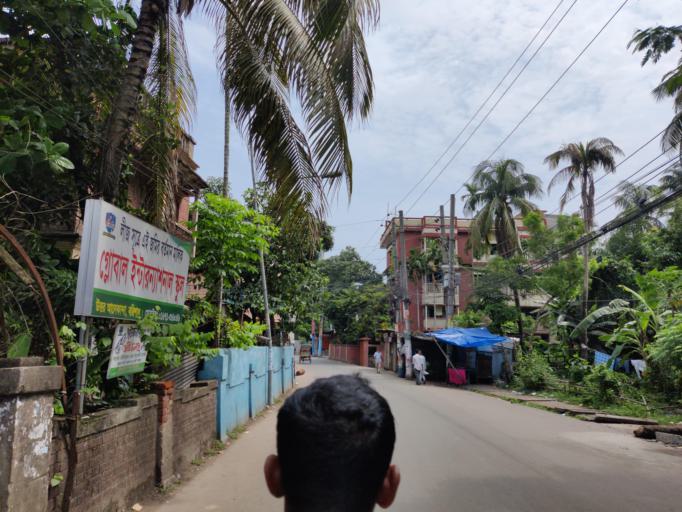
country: BD
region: Barisal
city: Barisal
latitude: 22.7024
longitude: 90.3652
